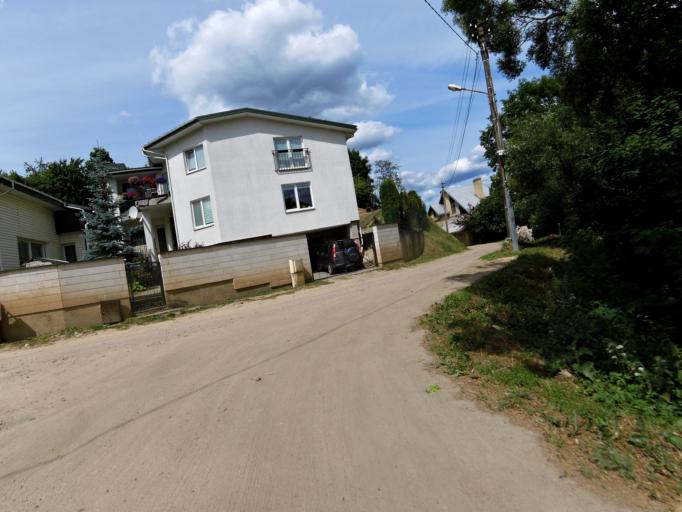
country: LT
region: Vilnius County
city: Rasos
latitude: 54.6714
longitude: 25.3176
